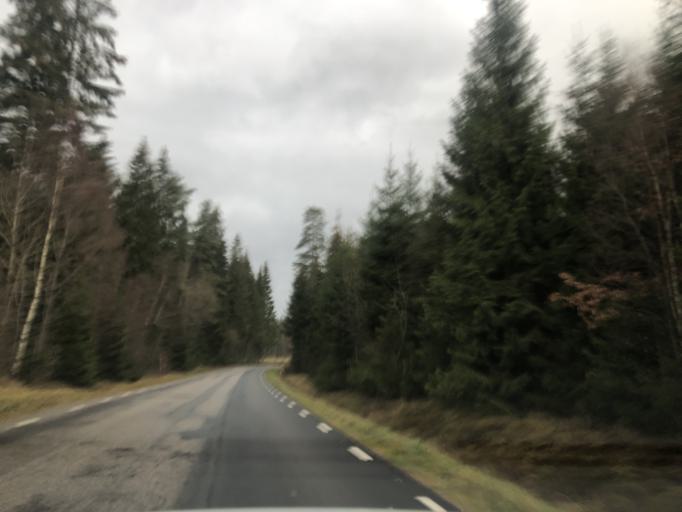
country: SE
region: Vaestra Goetaland
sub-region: Boras Kommun
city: Dalsjofors
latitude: 57.8158
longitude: 13.1975
